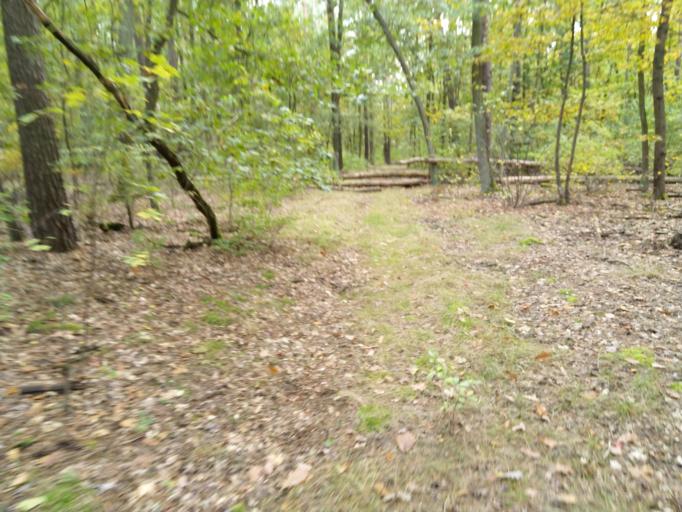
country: DE
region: Berlin
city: Rahnsdorf
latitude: 52.4530
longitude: 13.6604
